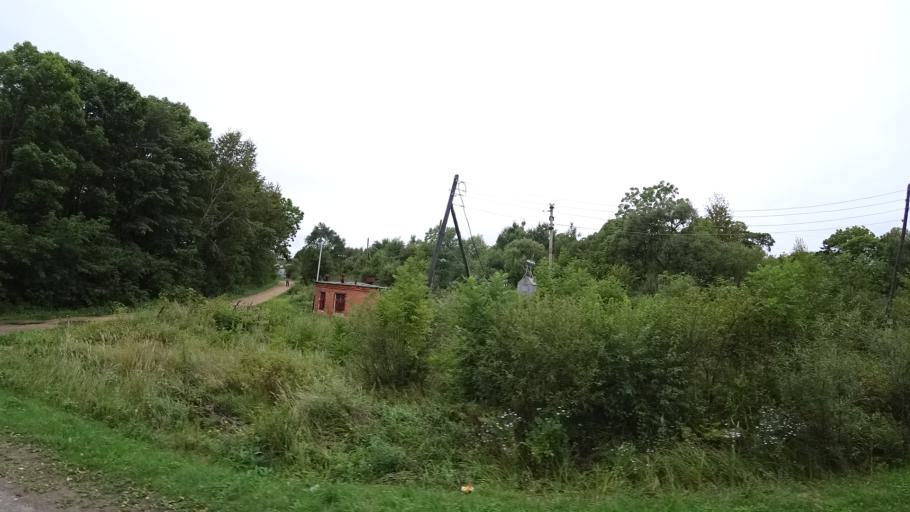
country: RU
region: Primorskiy
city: Rettikhovka
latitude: 44.1665
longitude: 132.7689
